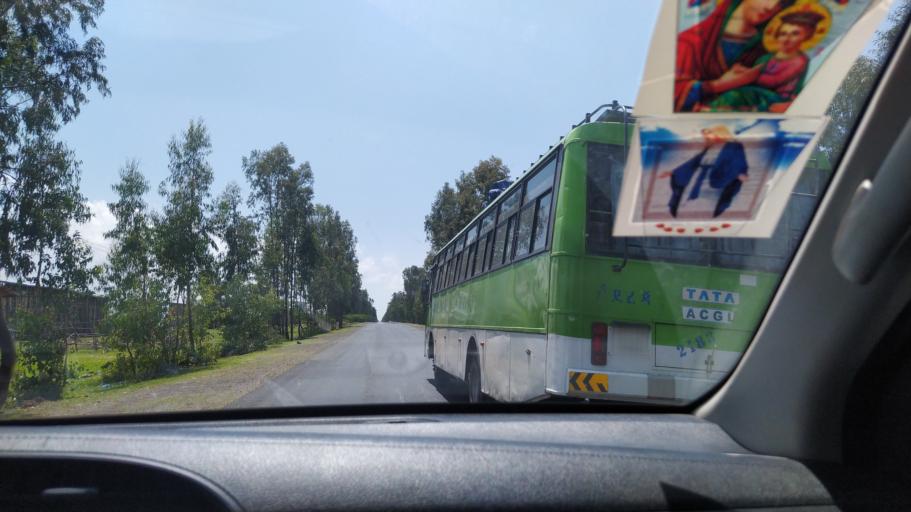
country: ET
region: Southern Nations, Nationalities, and People's Region
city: Butajira
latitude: 7.7871
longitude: 38.1434
